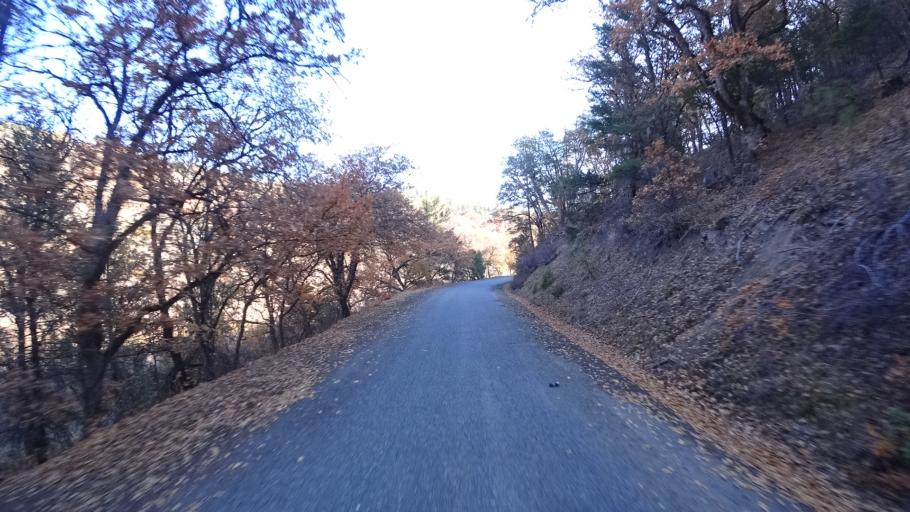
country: US
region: California
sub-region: Siskiyou County
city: Yreka
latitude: 41.8460
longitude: -122.9051
